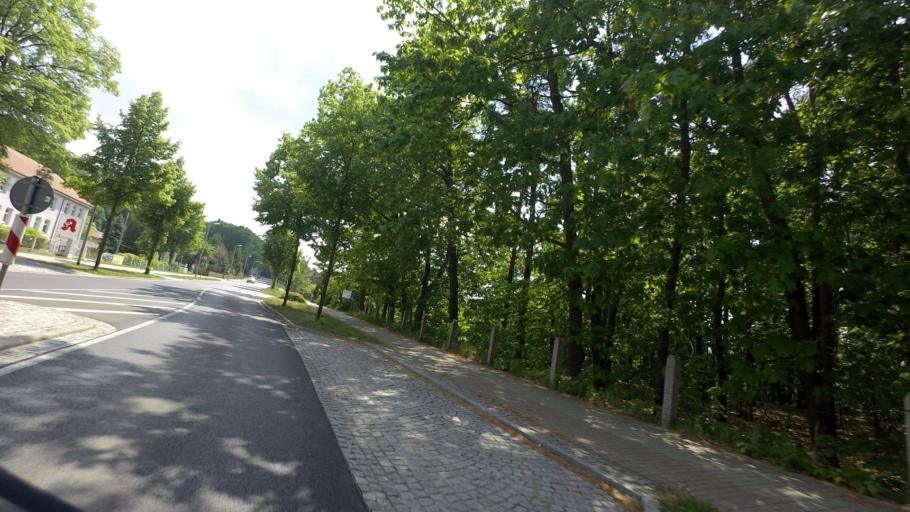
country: DE
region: Saxony
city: Rietschen
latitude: 51.3915
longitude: 14.7851
